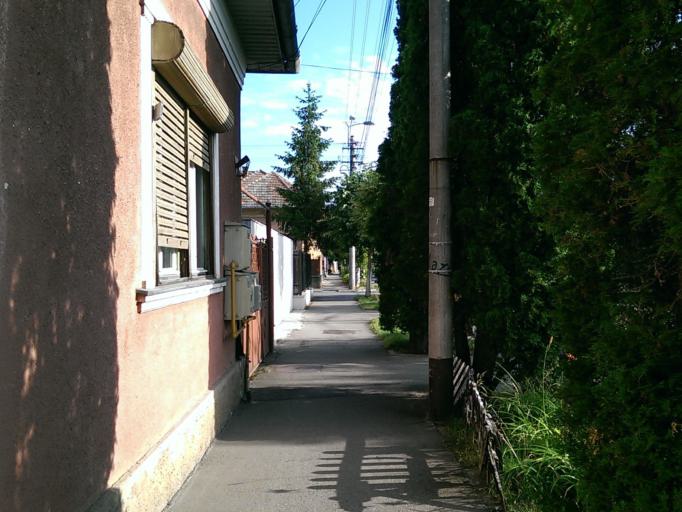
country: RO
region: Cluj
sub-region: Municipiul Cluj-Napoca
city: Cluj-Napoca
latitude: 46.7668
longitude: 23.6132
